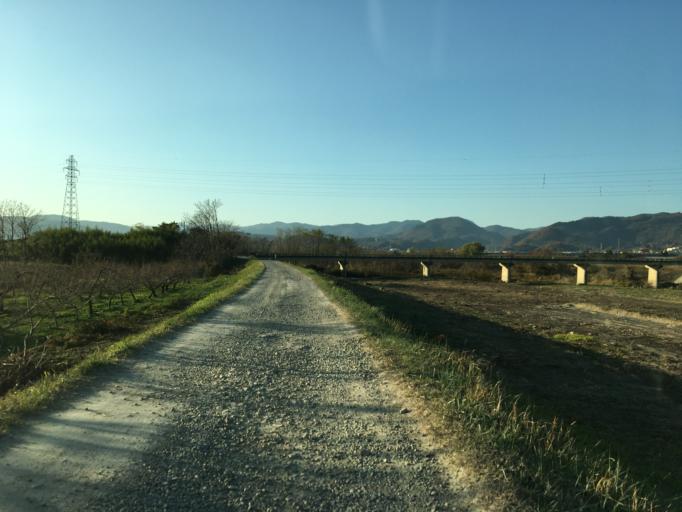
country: JP
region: Fukushima
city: Fukushima-shi
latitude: 37.8137
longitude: 140.4787
